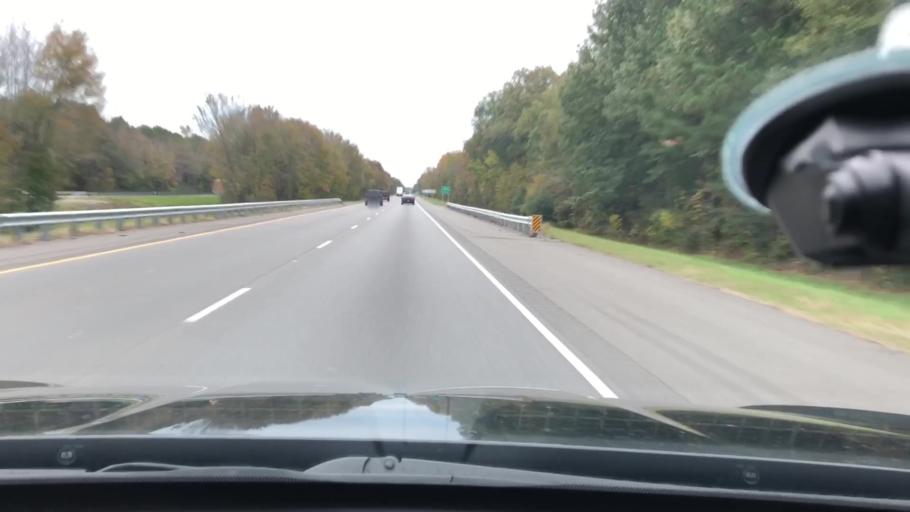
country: US
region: Arkansas
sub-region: Hempstead County
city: Hope
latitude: 33.6422
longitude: -93.6926
